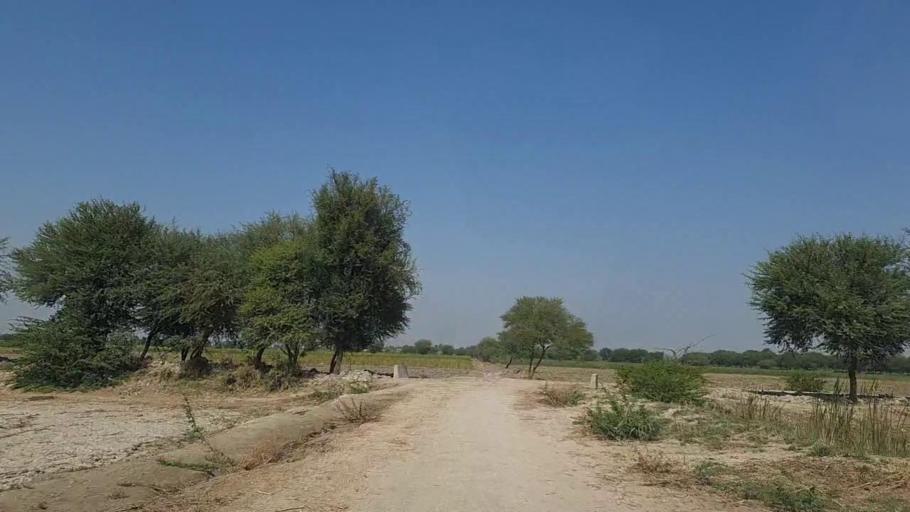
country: PK
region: Sindh
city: Naukot
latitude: 24.8790
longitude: 69.3838
